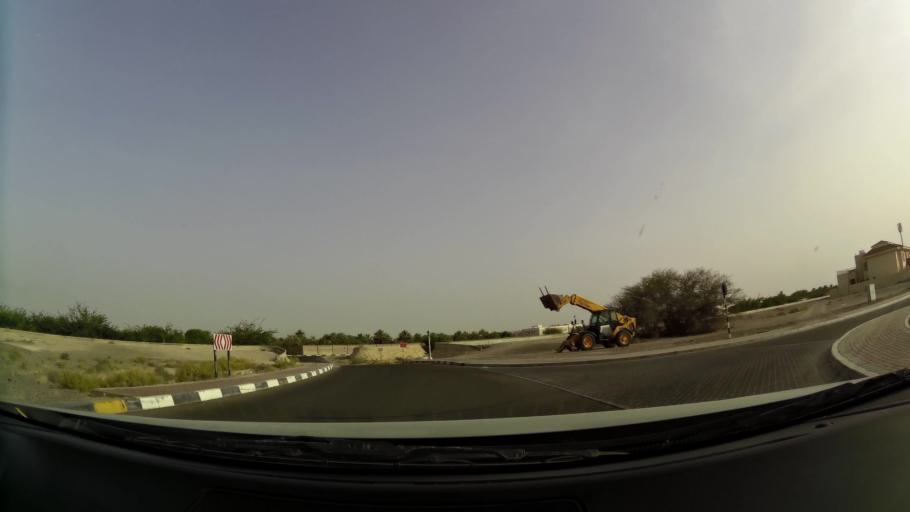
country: AE
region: Abu Dhabi
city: Al Ain
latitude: 24.2234
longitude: 55.7072
